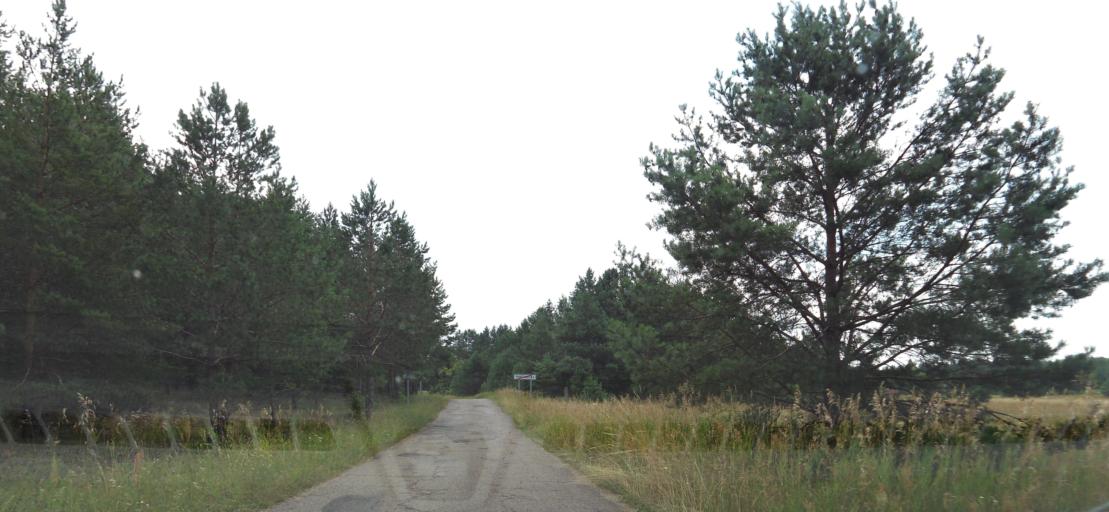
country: LT
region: Vilnius County
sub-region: Trakai
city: Rudiskes
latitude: 54.3961
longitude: 24.9596
